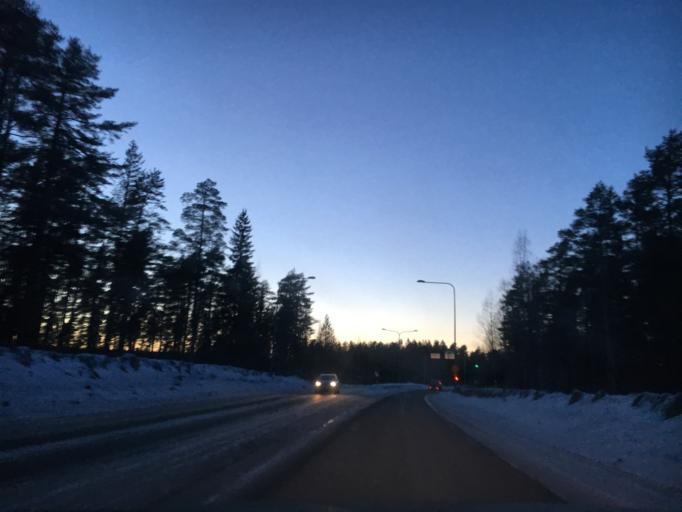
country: FI
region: Kainuu
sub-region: Kajaani
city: Kajaani
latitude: 64.2045
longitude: 27.7377
